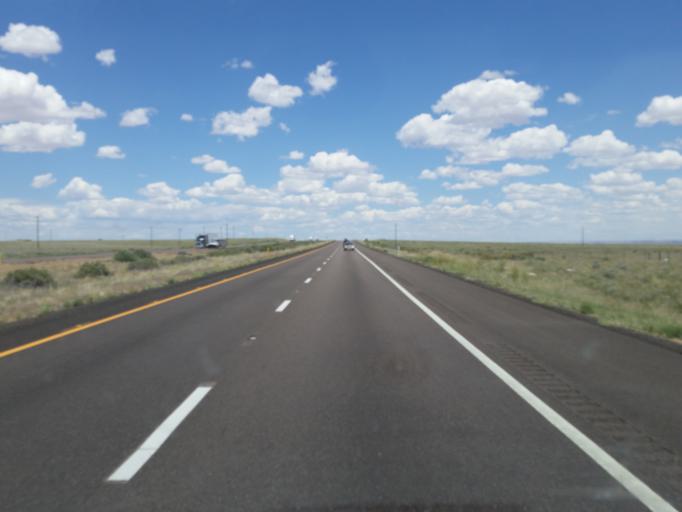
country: US
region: Arizona
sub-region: Navajo County
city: Holbrook
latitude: 34.9861
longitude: -110.0233
